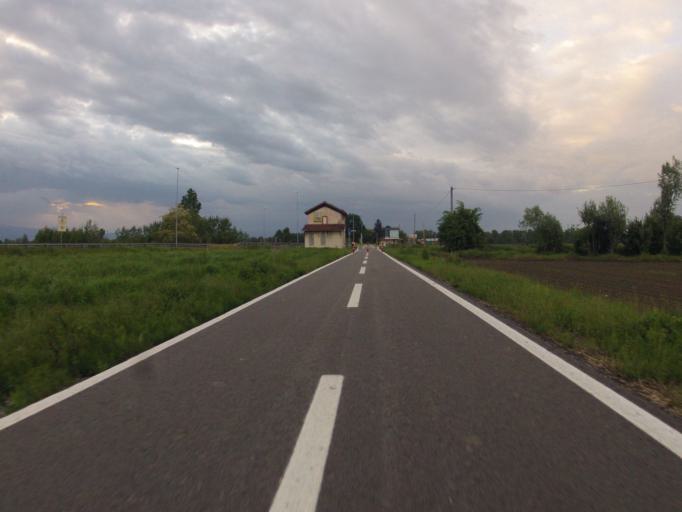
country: IT
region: Piedmont
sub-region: Provincia di Torino
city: Villafranca Piemonte
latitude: 44.8048
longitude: 7.5027
